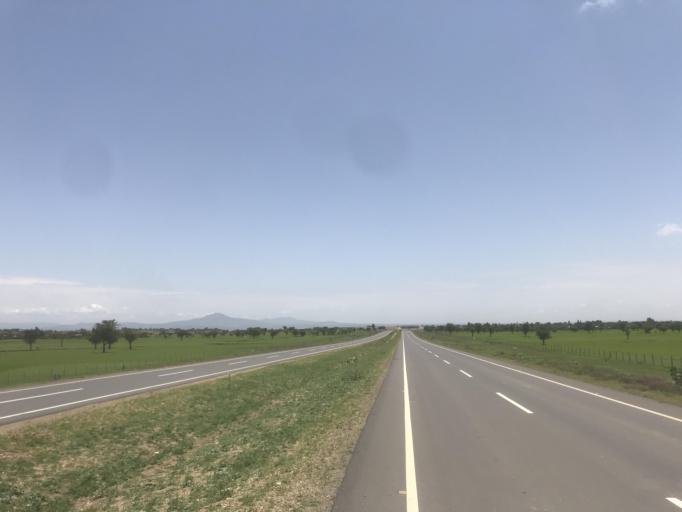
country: ET
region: Oromiya
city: Mojo
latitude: 8.4886
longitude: 39.0538
